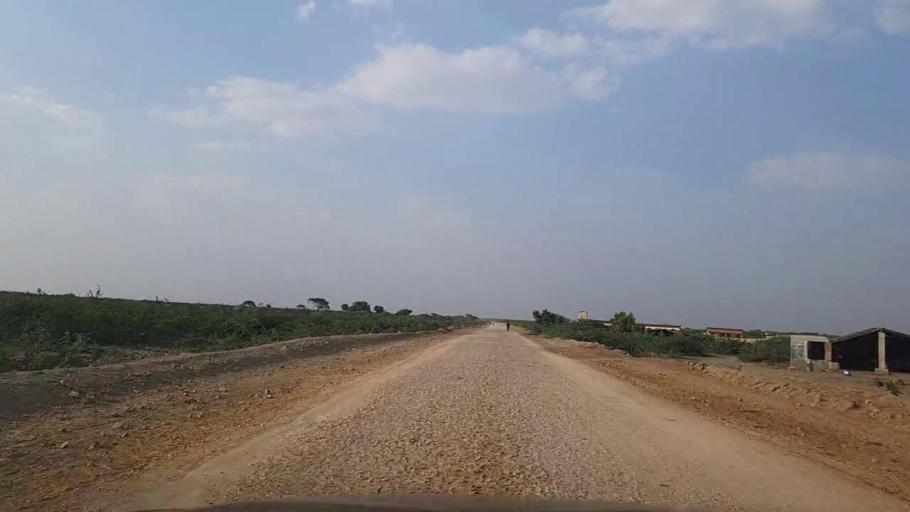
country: PK
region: Sindh
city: Gharo
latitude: 24.7991
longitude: 67.7442
